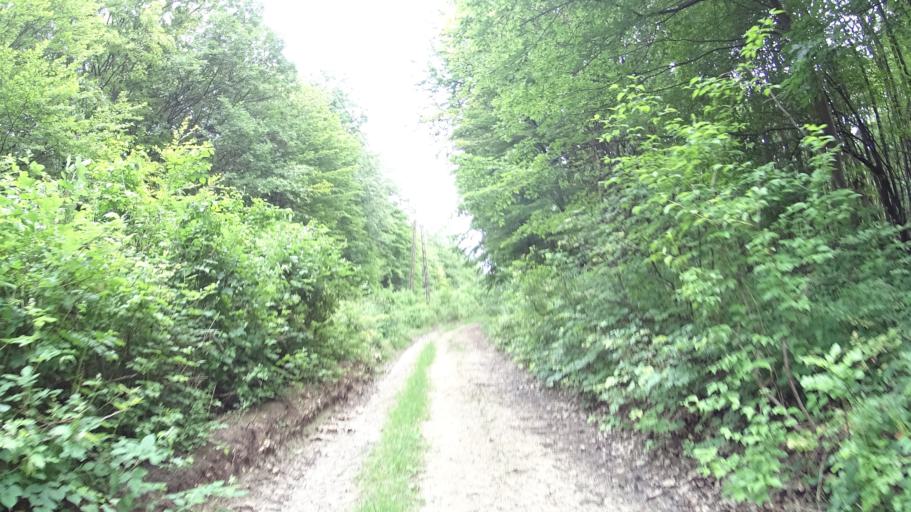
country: HU
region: Pest
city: Nagymaros
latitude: 47.7996
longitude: 18.9395
